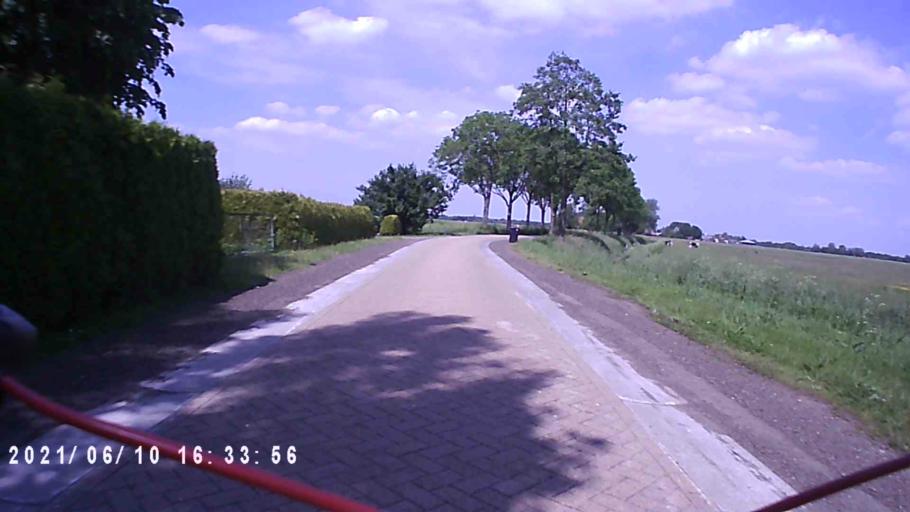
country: NL
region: Friesland
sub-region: Gemeente Achtkarspelen
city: Buitenpost
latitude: 53.2304
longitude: 6.1301
